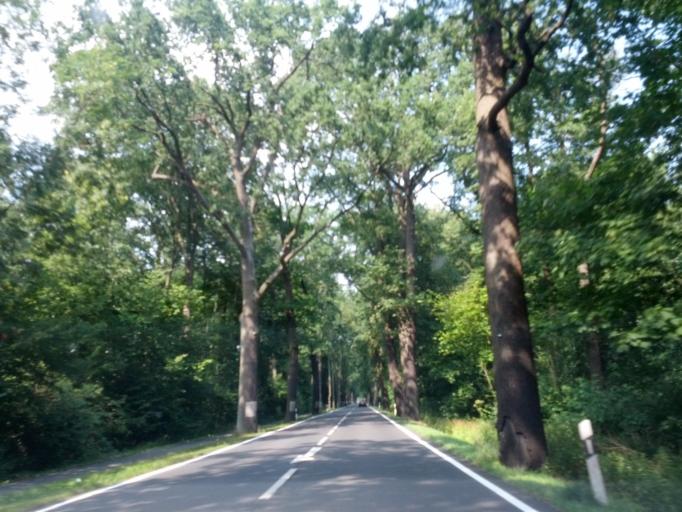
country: DE
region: Brandenburg
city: Nauen
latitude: 52.6651
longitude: 12.9266
